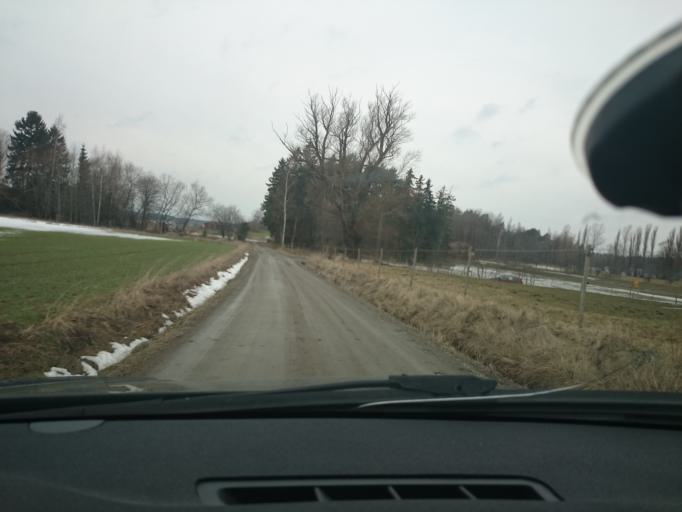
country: SE
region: OEstergoetland
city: Lindo
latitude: 58.5628
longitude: 16.2624
